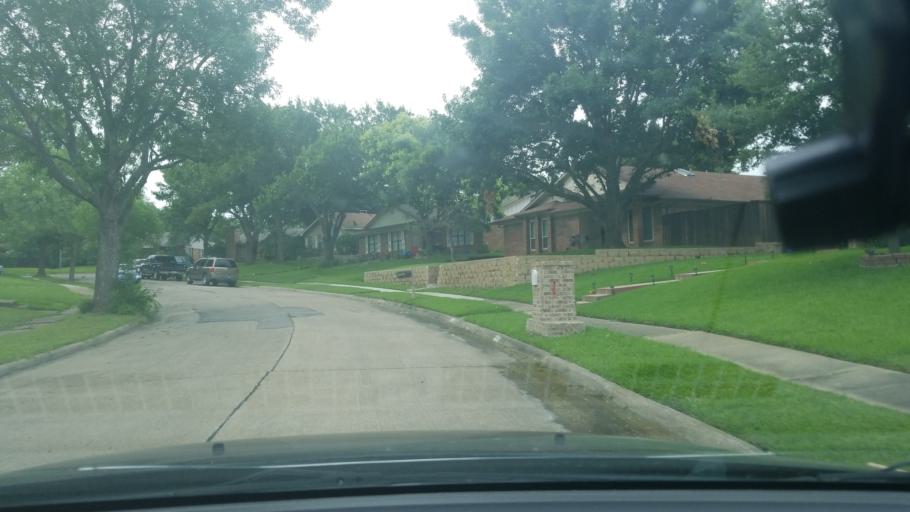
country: US
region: Texas
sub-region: Dallas County
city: Mesquite
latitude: 32.7855
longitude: -96.6440
